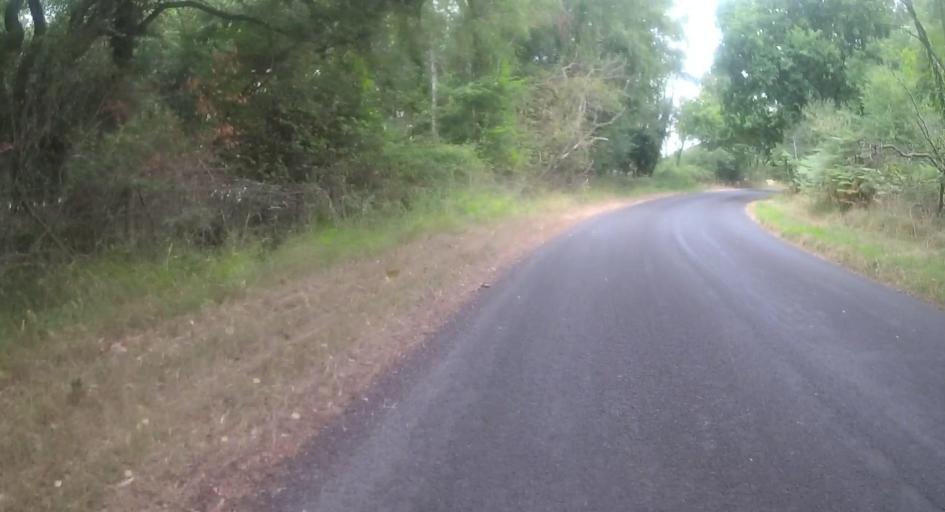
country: GB
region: England
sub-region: Dorset
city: Wareham
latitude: 50.6464
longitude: -2.0988
